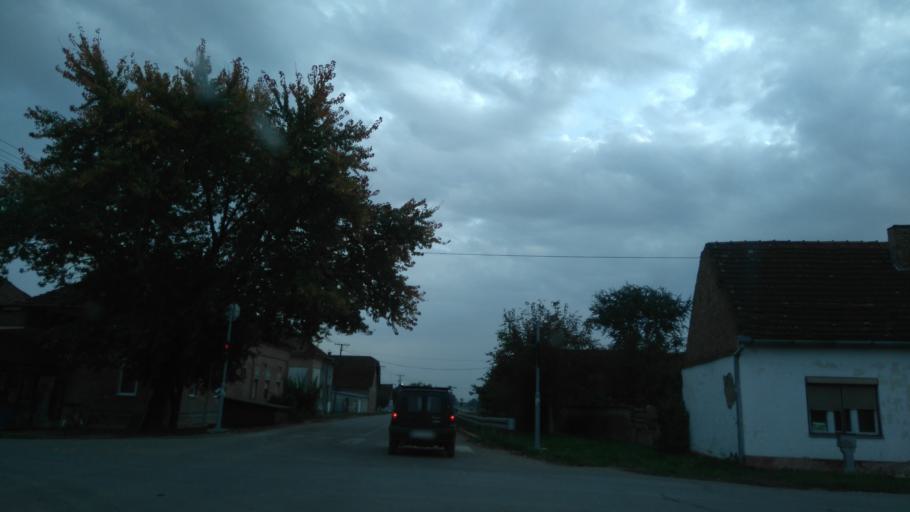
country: RS
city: Mol
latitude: 45.7637
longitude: 20.1243
